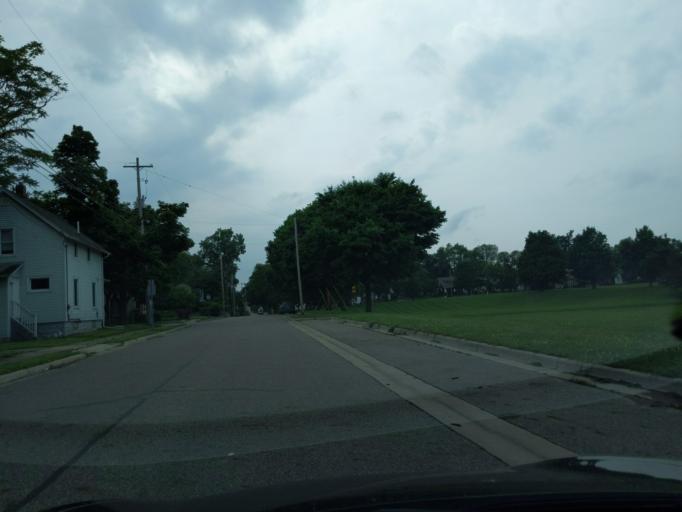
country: US
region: Michigan
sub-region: Ingham County
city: Lansing
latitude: 42.7446
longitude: -84.5638
